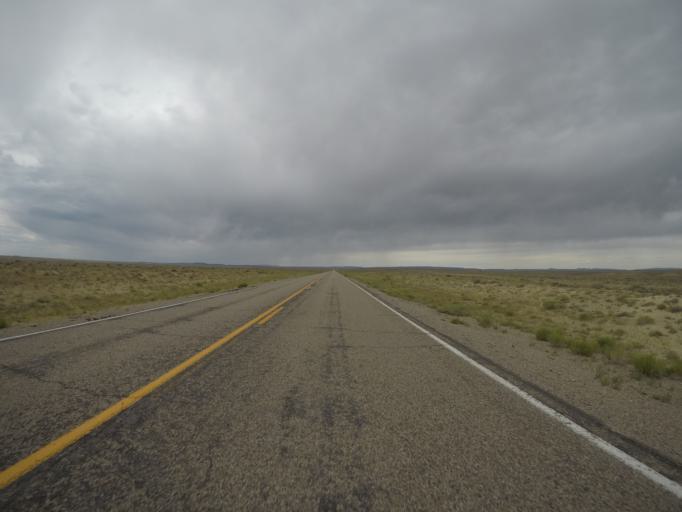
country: US
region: Wyoming
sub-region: Lincoln County
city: Kemmerer
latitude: 41.9640
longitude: -110.1547
